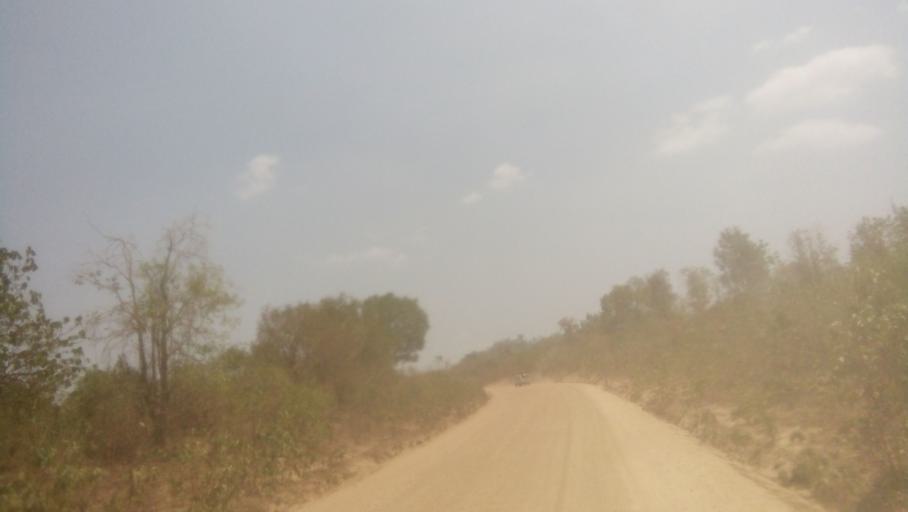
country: TH
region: Tak
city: Tha Song Yang
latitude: 17.2885
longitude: 97.8310
